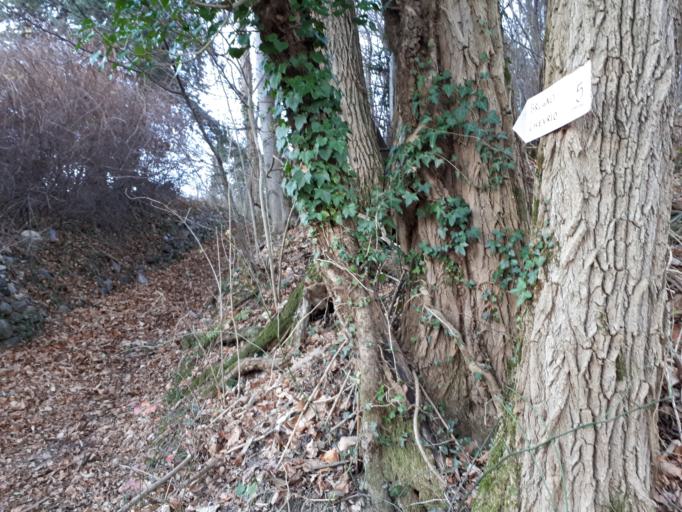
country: IT
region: Lombardy
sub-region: Provincia di Como
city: Cadenabbia
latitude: 45.9679
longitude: 9.2412
